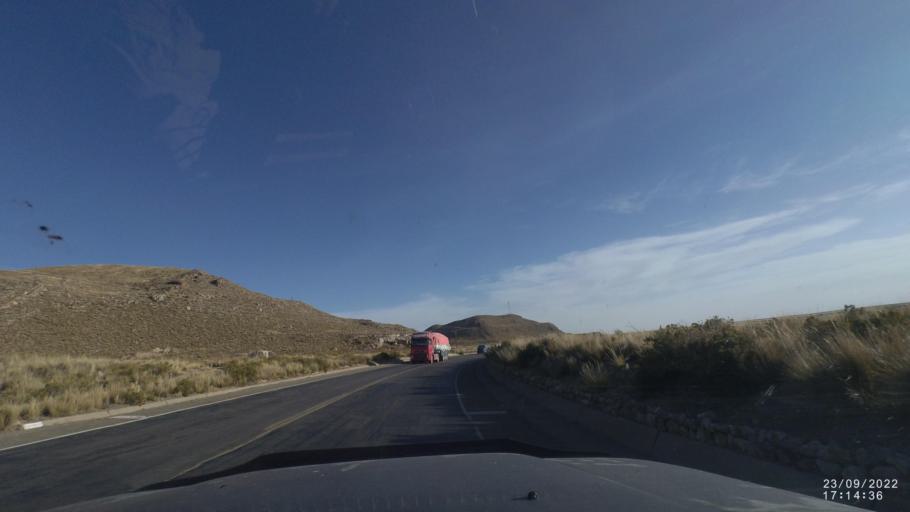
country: BO
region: Oruro
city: Challapata
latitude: -18.7240
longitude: -66.8665
